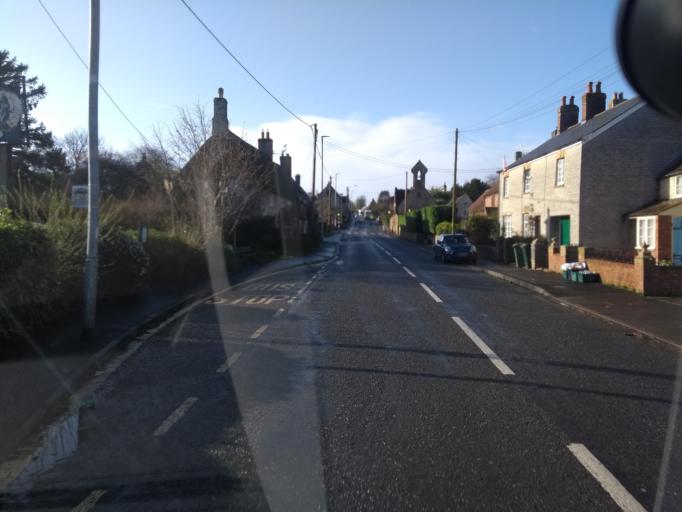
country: GB
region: England
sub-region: Somerset
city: Yeovil
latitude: 50.9765
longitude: -2.6079
